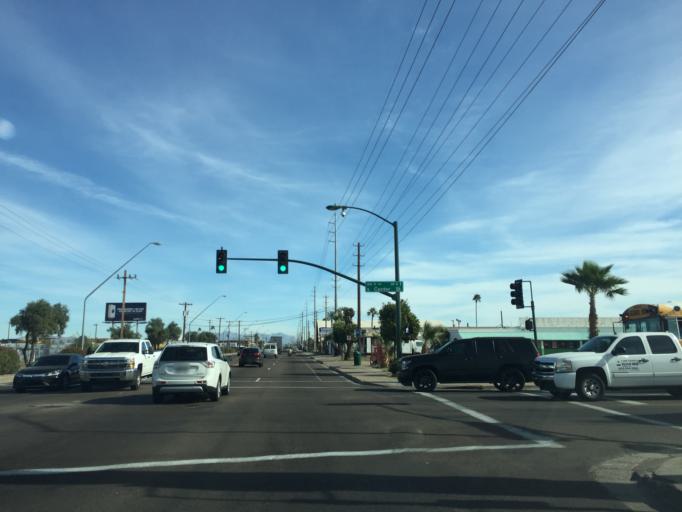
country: US
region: Arizona
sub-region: Maricopa County
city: Mesa
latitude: 33.4078
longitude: -111.8317
